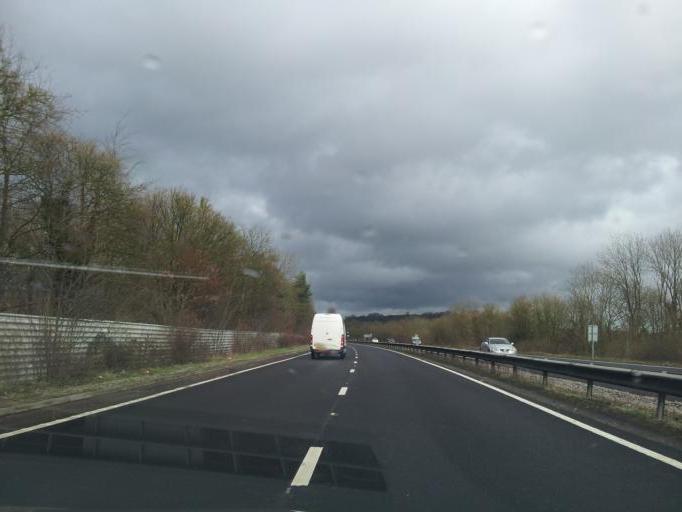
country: GB
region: England
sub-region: Somerset
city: Wincanton
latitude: 51.0494
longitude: -2.4098
